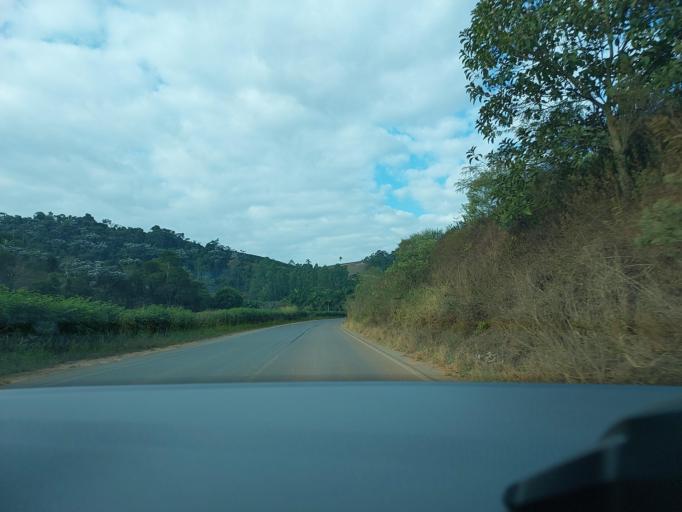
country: BR
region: Minas Gerais
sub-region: Vicosa
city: Vicosa
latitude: -20.8367
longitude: -42.6938
